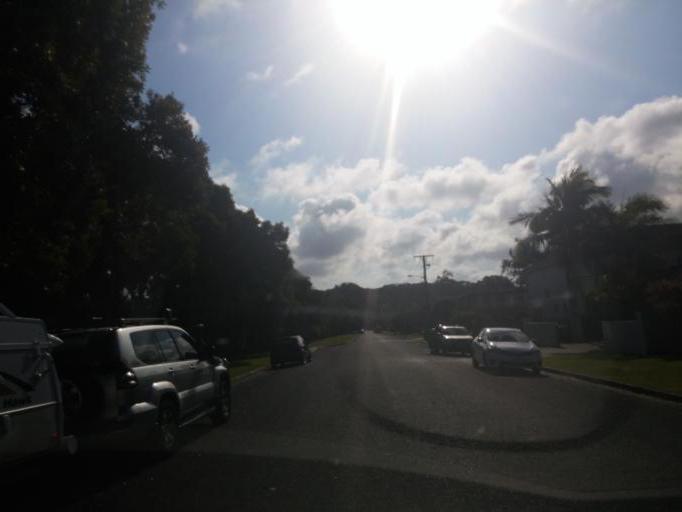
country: AU
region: New South Wales
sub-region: Coffs Harbour
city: Coffs Harbour
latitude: -30.2922
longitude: 153.1376
